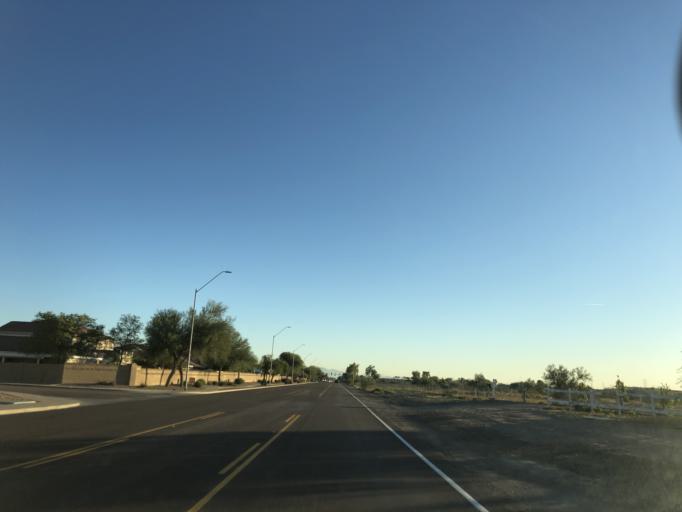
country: US
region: Arizona
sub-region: Maricopa County
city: Sun City West
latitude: 33.6932
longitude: -112.2897
